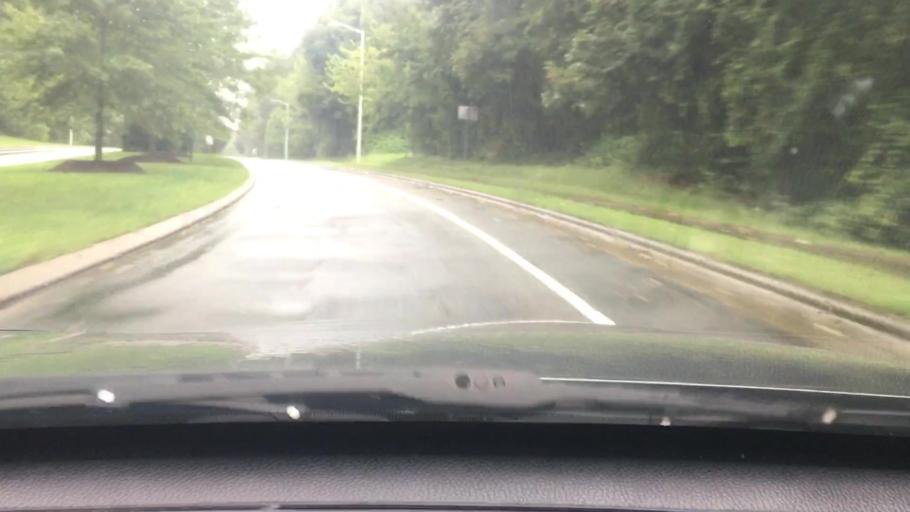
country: US
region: North Carolina
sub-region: Alamance County
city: Burlington
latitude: 36.0886
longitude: -79.4607
